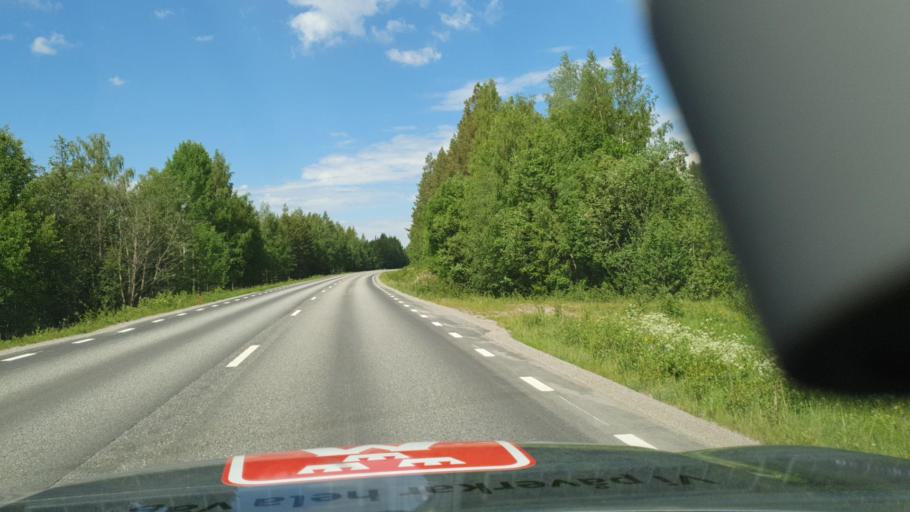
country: SE
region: Vaesternorrland
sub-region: Solleftea Kommun
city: As
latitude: 63.5176
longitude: 16.8366
